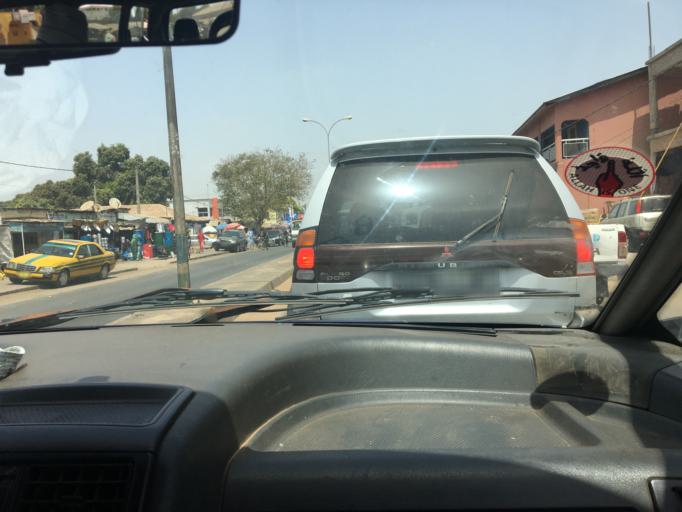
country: GM
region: Western
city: Abuko
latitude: 13.4120
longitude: -16.6707
